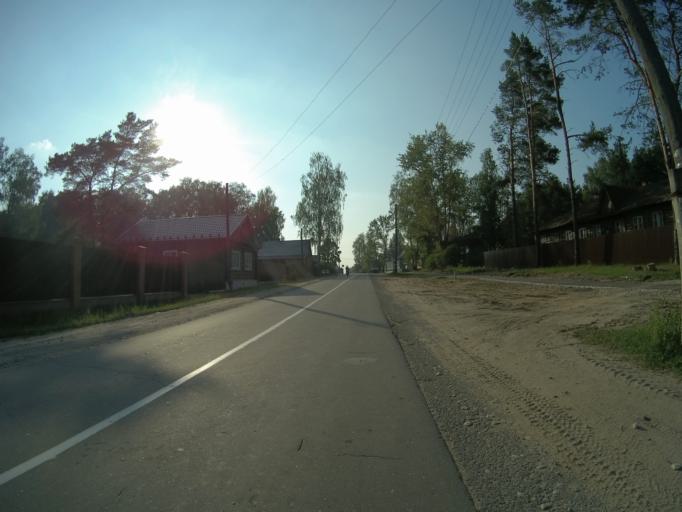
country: RU
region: Vladimir
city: Sudogda
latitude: 56.0708
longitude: 40.7923
